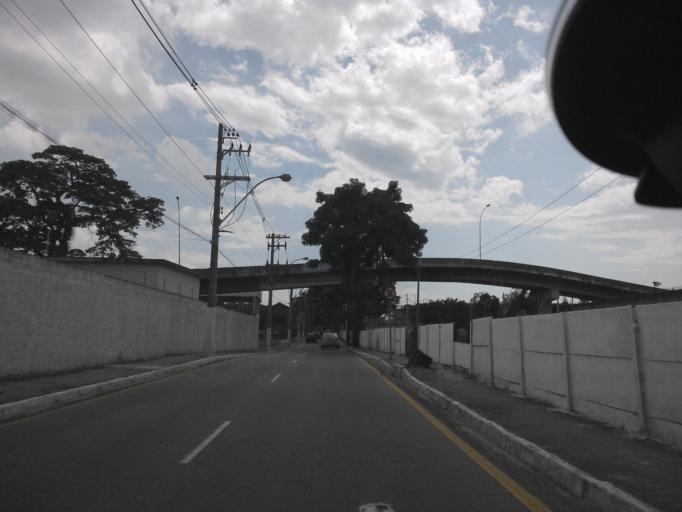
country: BR
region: Sao Paulo
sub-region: Taubate
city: Taubate
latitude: -23.0210
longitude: -45.5575
